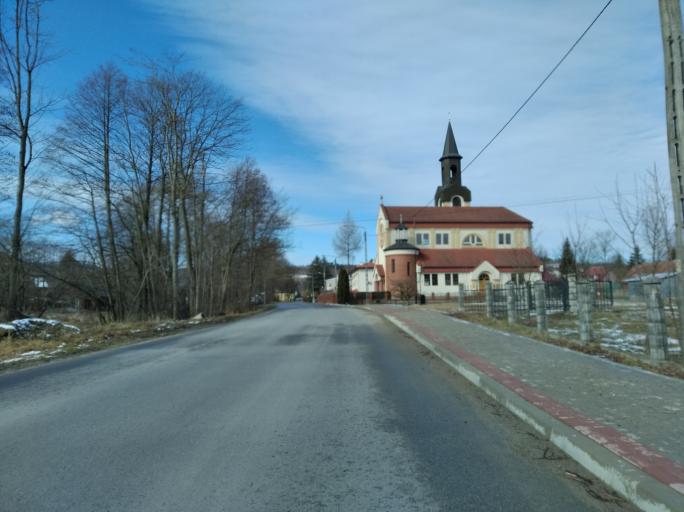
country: PL
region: Subcarpathian Voivodeship
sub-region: Powiat brzozowski
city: Jasienica Rosielna
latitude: 49.7537
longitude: 21.8996
